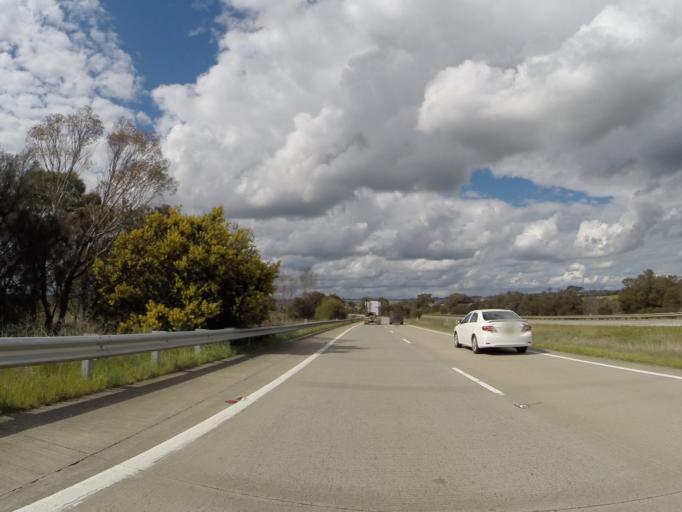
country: AU
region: New South Wales
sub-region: Yass Valley
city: Murrumbateman
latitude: -34.7931
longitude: 149.1674
